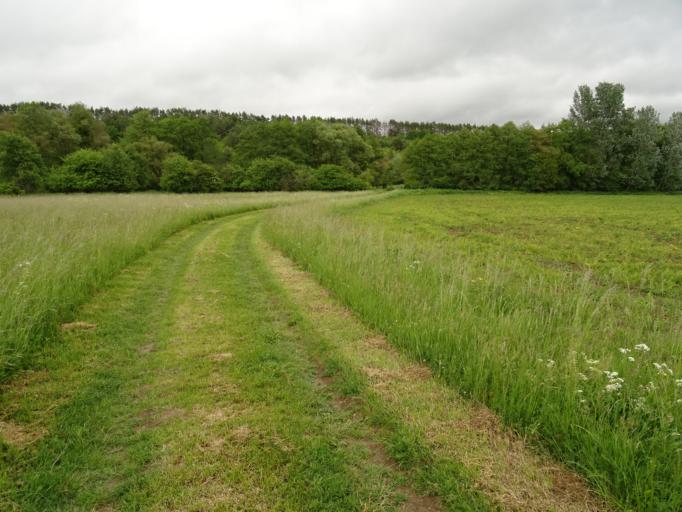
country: HU
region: Borsod-Abauj-Zemplen
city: Gonc
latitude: 48.4980
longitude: 21.4513
